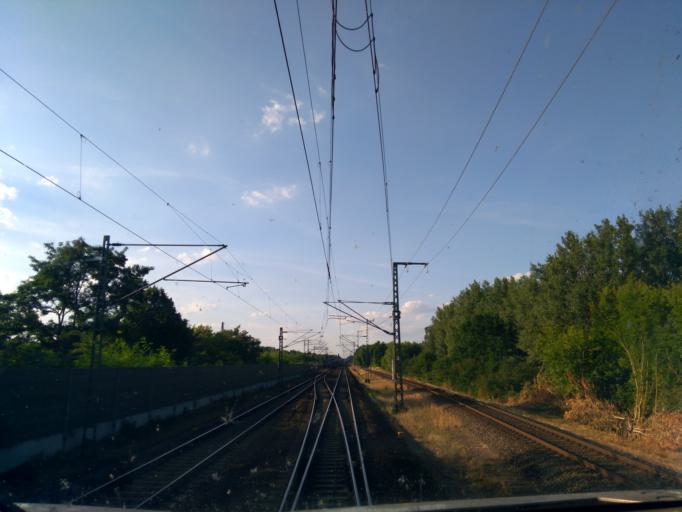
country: DE
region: Brandenburg
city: Wittenberge
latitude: 53.0128
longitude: 11.7610
